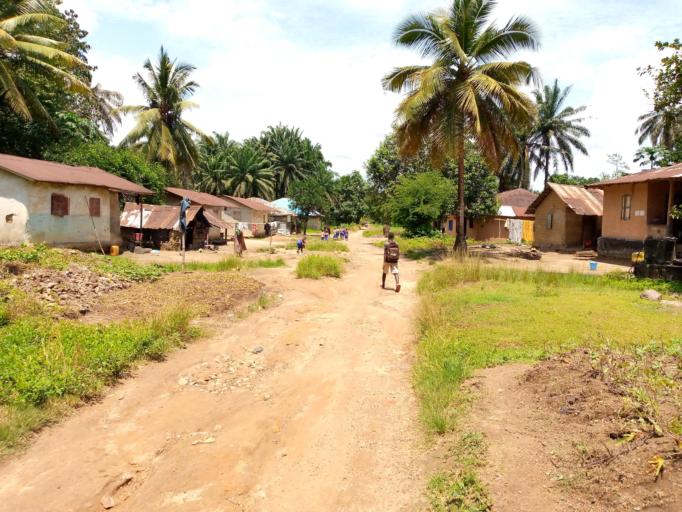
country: SL
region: Northern Province
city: Magburaka
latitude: 8.7103
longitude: -11.9593
